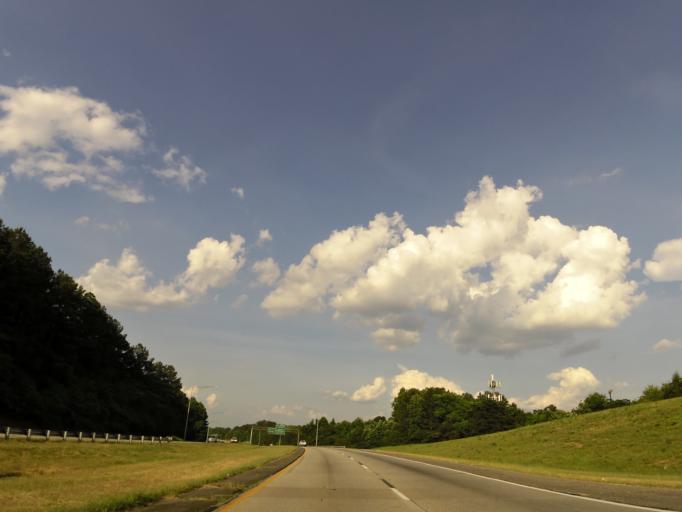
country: US
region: Alabama
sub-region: Jefferson County
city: Irondale
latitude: 33.5854
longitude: -86.6737
